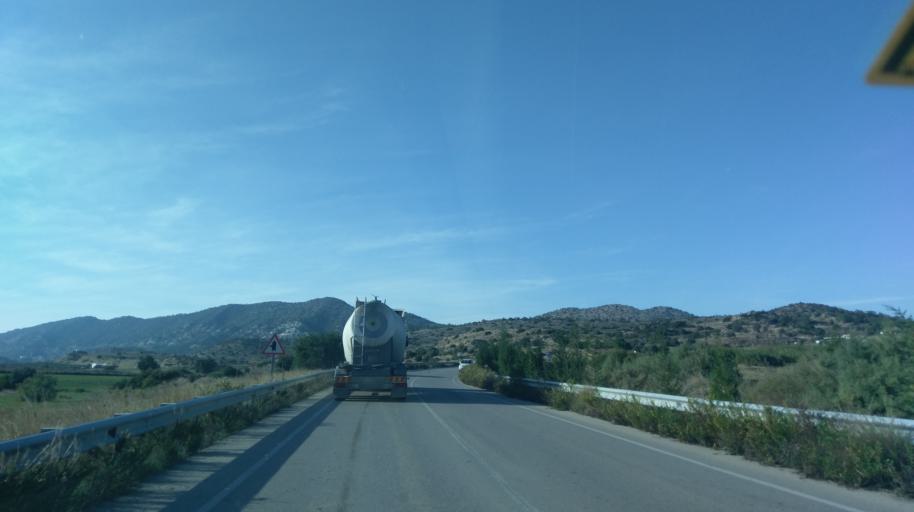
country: CY
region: Ammochostos
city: Lefkonoiko
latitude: 35.3304
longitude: 33.7216
